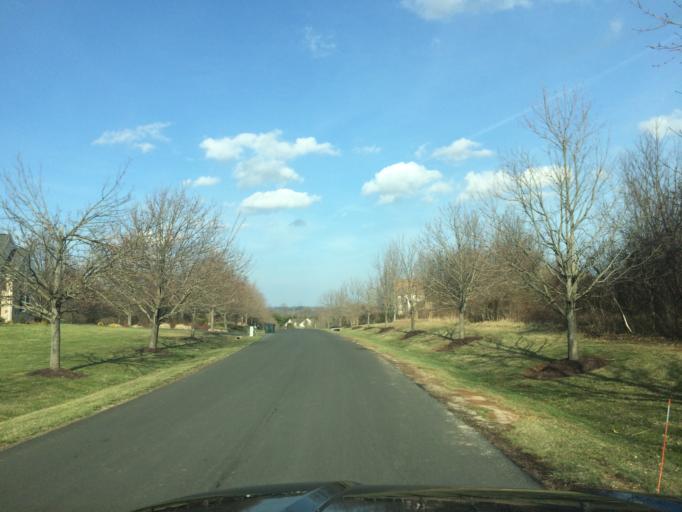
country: US
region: Maryland
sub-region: Carroll County
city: Sykesville
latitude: 39.2804
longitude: -76.9828
